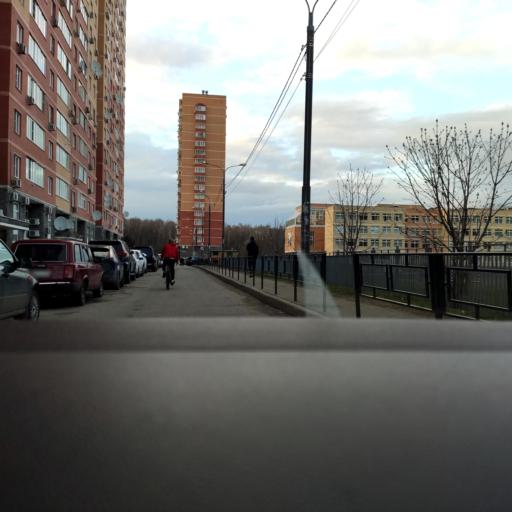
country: RU
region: Moskovskaya
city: Vidnoye
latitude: 55.5430
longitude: 37.7254
